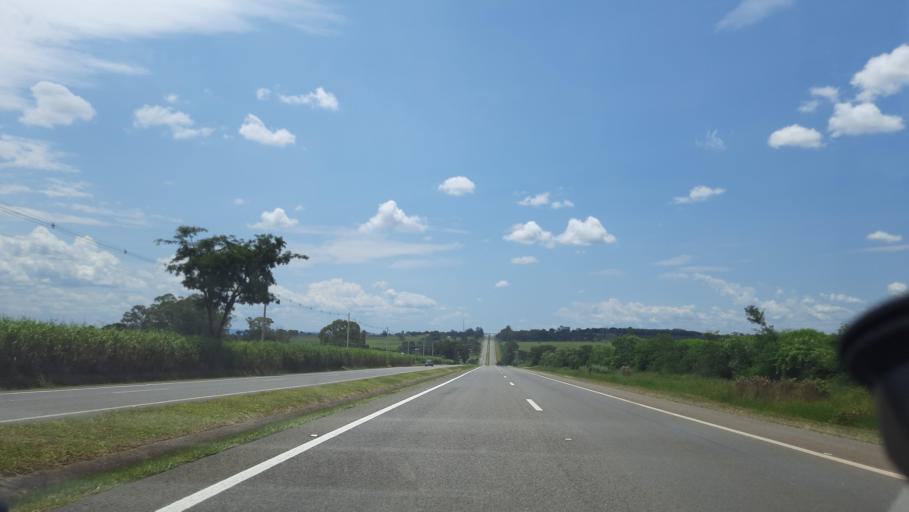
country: BR
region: Sao Paulo
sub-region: Mococa
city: Mococa
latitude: -21.5957
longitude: -47.0402
